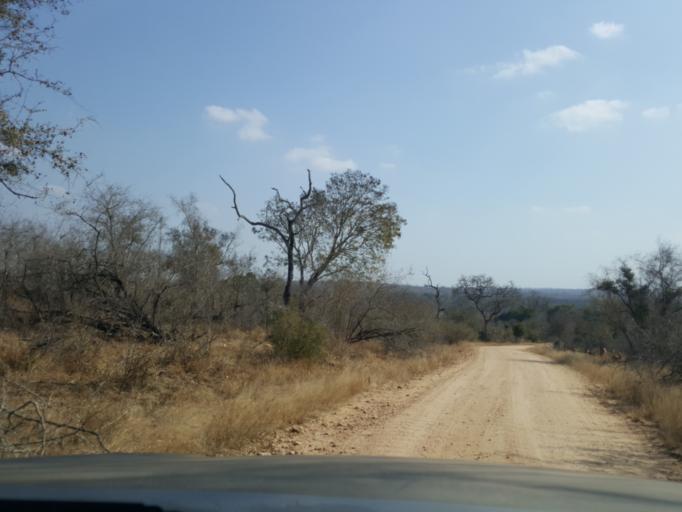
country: ZA
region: Mpumalanga
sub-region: Ehlanzeni District
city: Komatipoort
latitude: -25.2730
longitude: 31.7846
